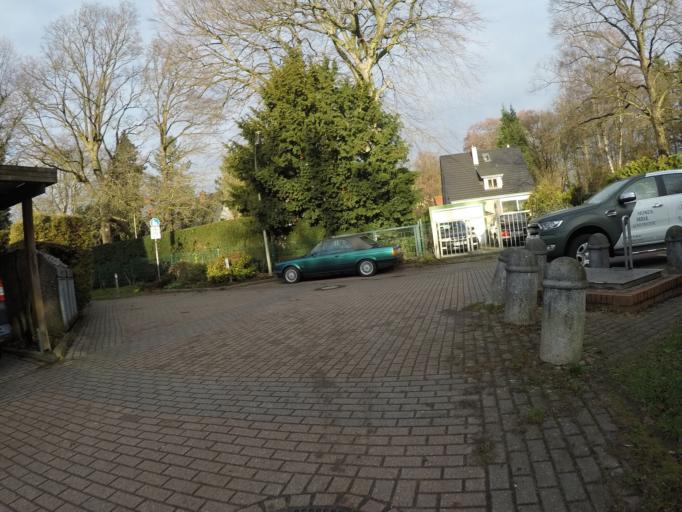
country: DE
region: Hamburg
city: Hamburg-Nord
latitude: 53.6059
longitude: 9.9650
